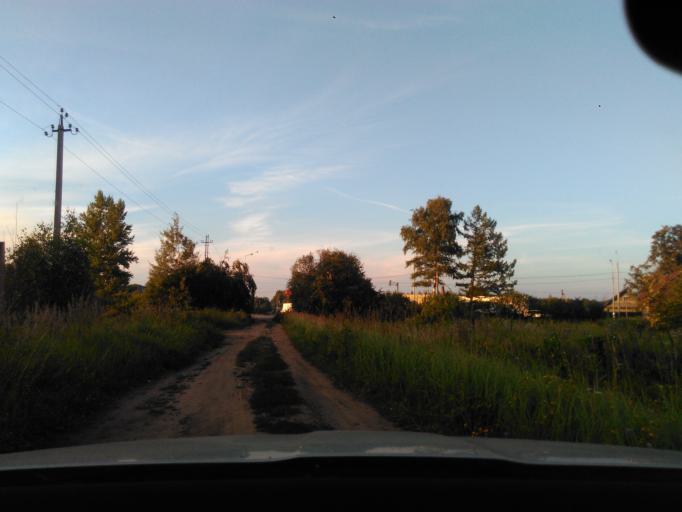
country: RU
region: Moskovskaya
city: Spas-Zaulok
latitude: 56.4981
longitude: 36.5518
